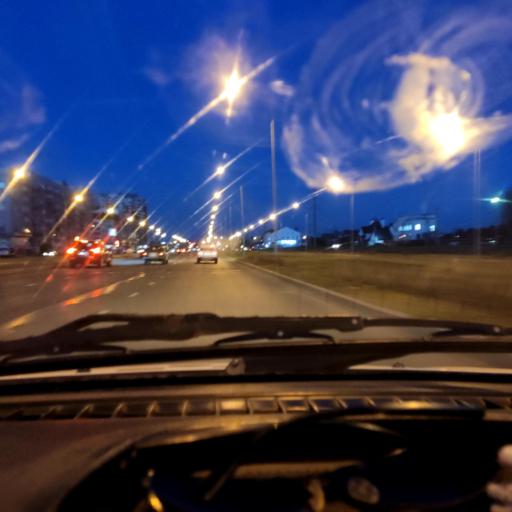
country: RU
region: Samara
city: Tol'yatti
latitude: 53.5419
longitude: 49.3658
